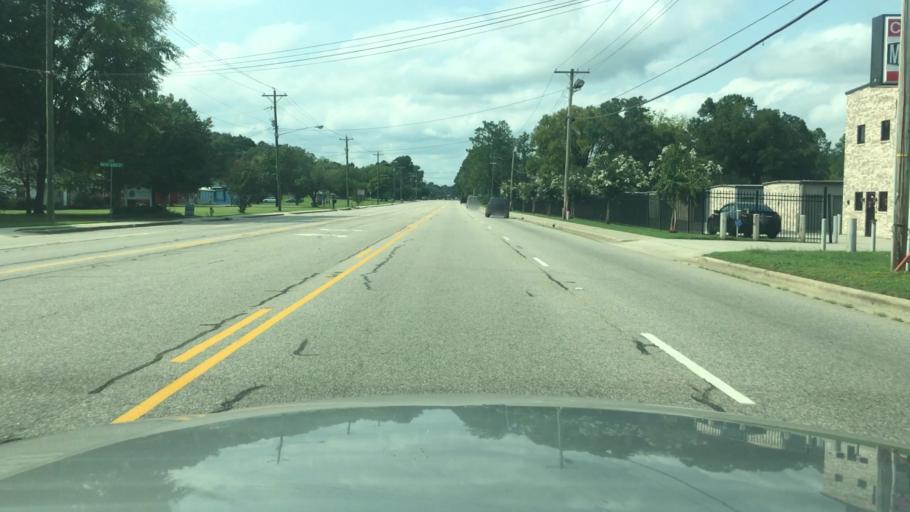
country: US
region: North Carolina
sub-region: Cumberland County
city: Vander
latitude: 35.0154
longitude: -78.8375
